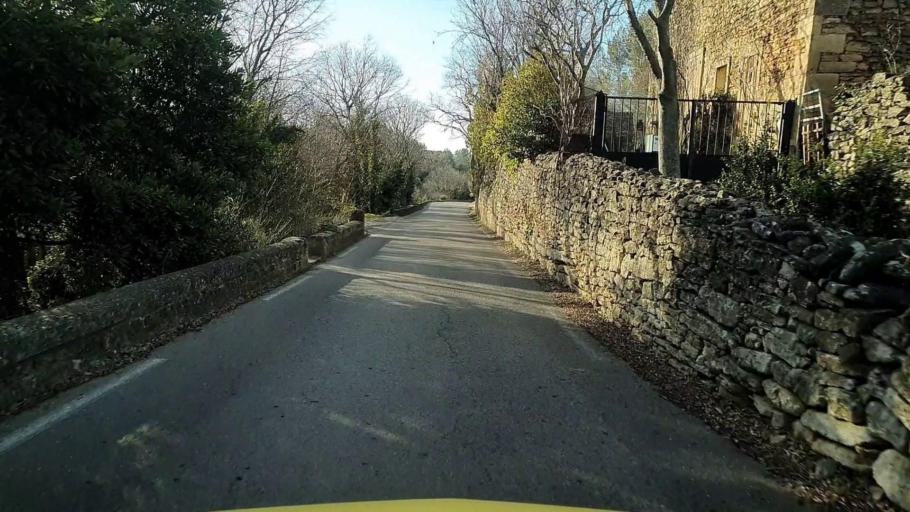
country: FR
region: Languedoc-Roussillon
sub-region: Departement du Gard
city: Castillon-du-Gard
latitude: 43.9676
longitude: 4.5548
